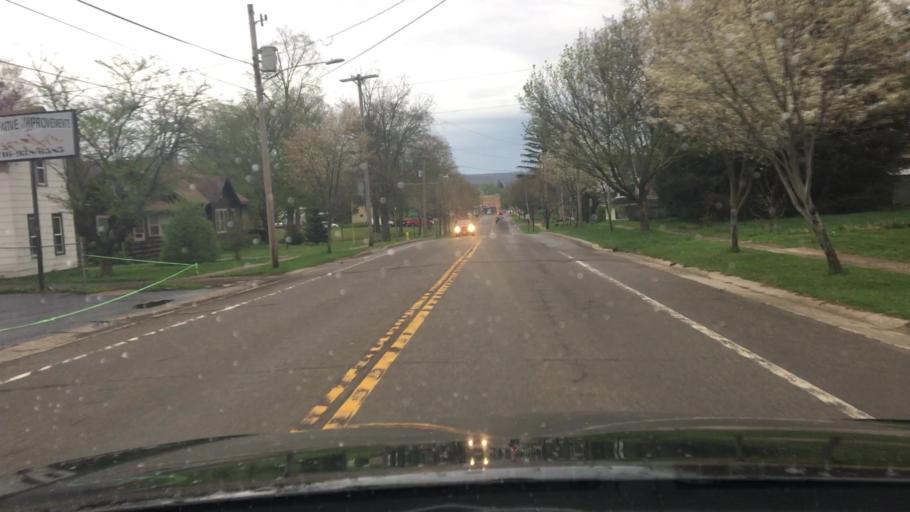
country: US
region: New York
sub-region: Cattaraugus County
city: Little Valley
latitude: 42.2517
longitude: -78.8032
